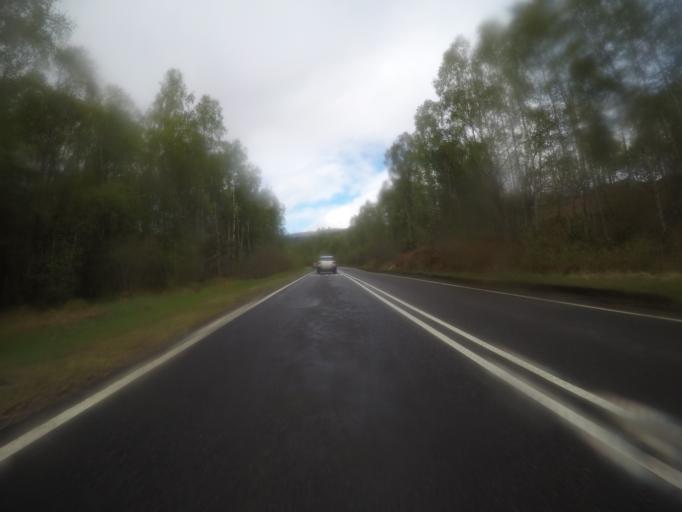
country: GB
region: Scotland
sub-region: Highland
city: Spean Bridge
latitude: 57.0826
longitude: -4.8988
